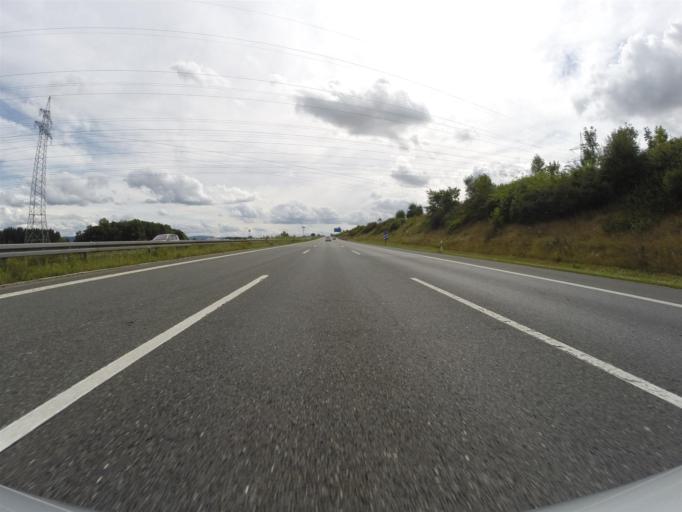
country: DE
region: Bavaria
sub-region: Upper Franconia
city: Munchberg
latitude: 50.2118
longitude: 11.7800
